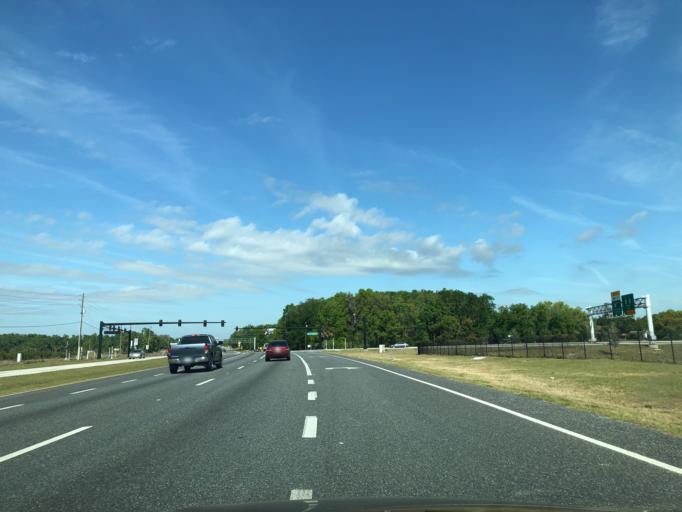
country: US
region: Florida
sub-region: Orange County
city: Zellwood
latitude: 28.6960
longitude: -81.5614
